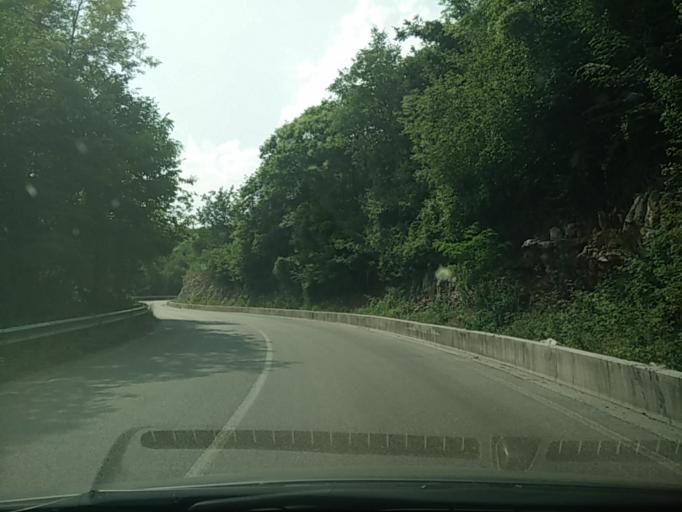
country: IT
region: Friuli Venezia Giulia
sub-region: Provincia di Pordenone
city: Aviano-Castello
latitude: 46.0708
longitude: 12.5535
